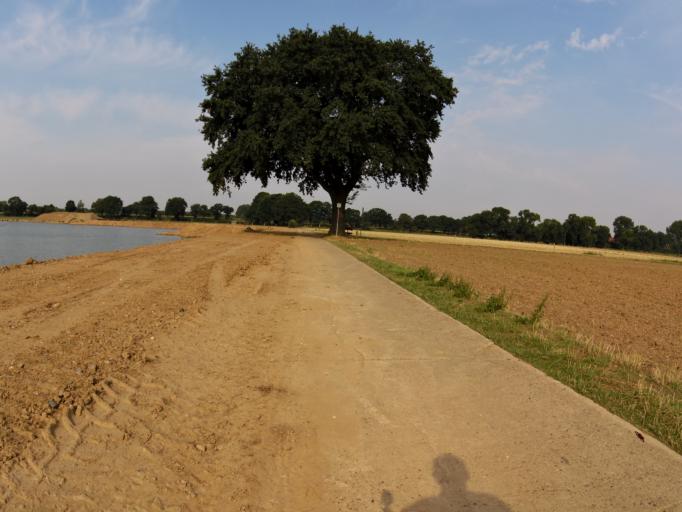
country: DE
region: Lower Saxony
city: Raddestorf
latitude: 52.4691
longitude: 9.0143
